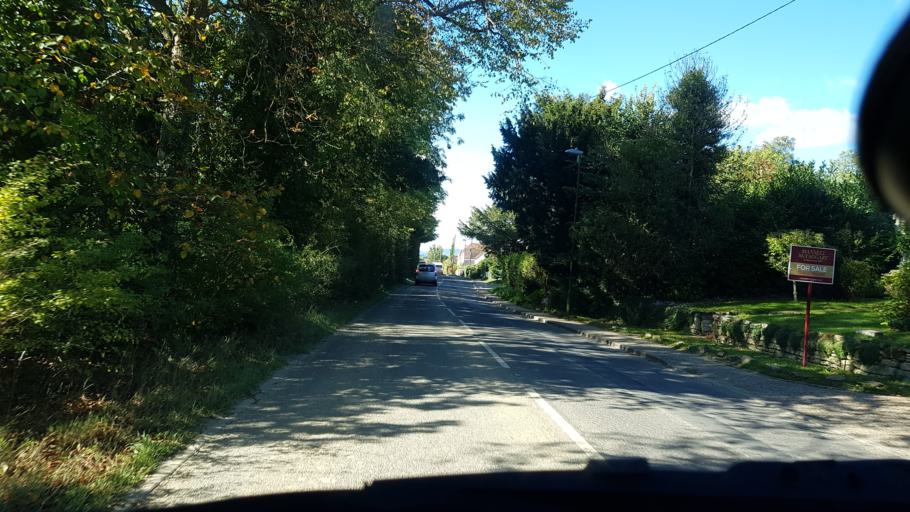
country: GB
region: England
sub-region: West Sussex
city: Billingshurst
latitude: 51.0222
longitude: -0.4453
